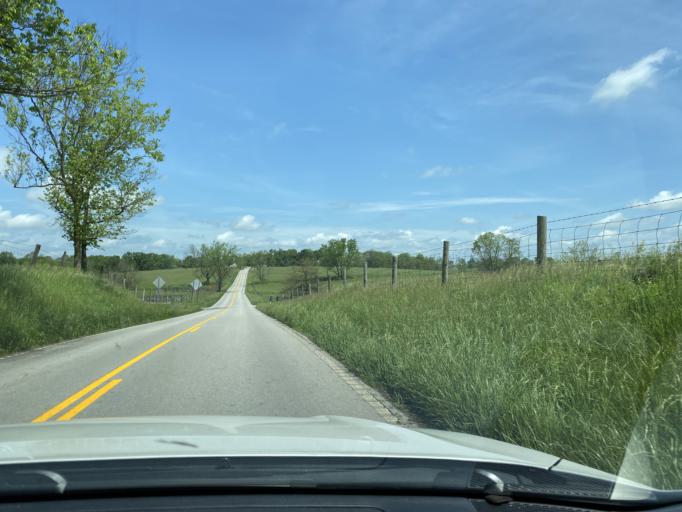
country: US
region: Kentucky
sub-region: Scott County
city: Georgetown
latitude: 38.2467
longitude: -84.5870
